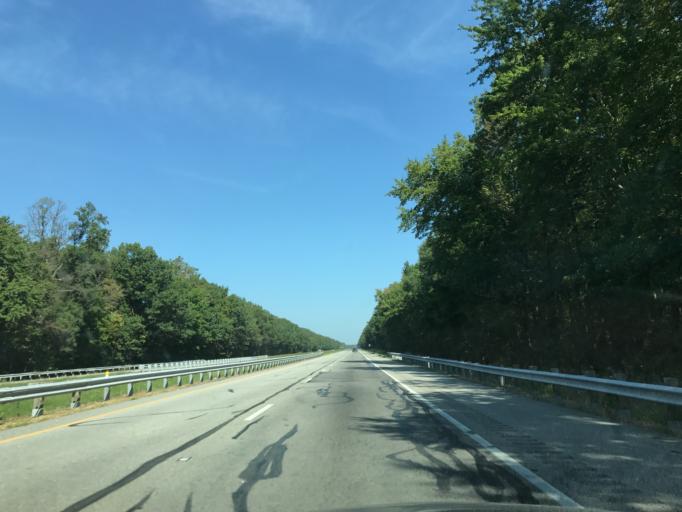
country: US
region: Delaware
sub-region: New Castle County
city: Townsend
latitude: 39.2992
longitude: -75.8518
